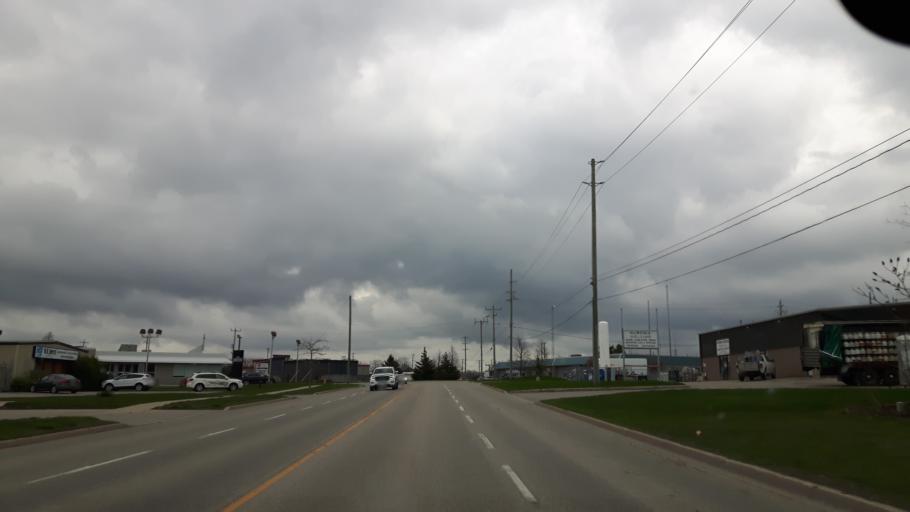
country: CA
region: Ontario
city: Goderich
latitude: 43.7316
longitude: -81.6969
